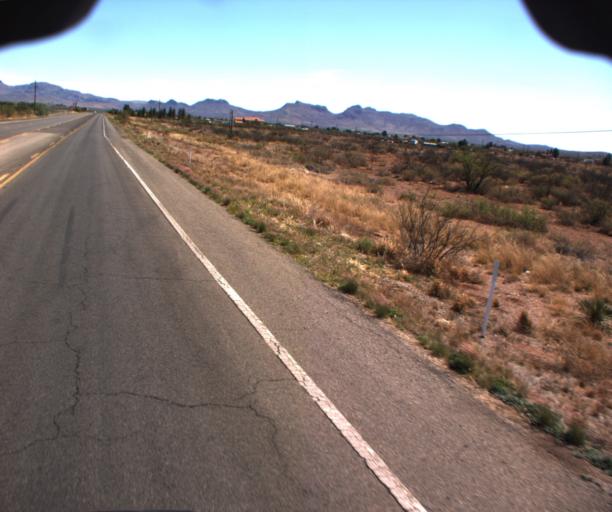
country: US
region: Arizona
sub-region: Cochise County
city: Douglas
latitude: 31.3627
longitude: -109.5436
